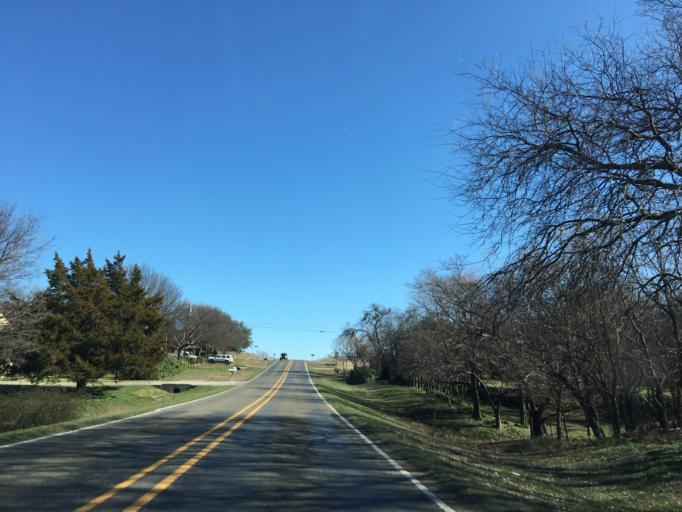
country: US
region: Texas
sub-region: Collin County
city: Prosper
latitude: 33.2360
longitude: -96.7964
